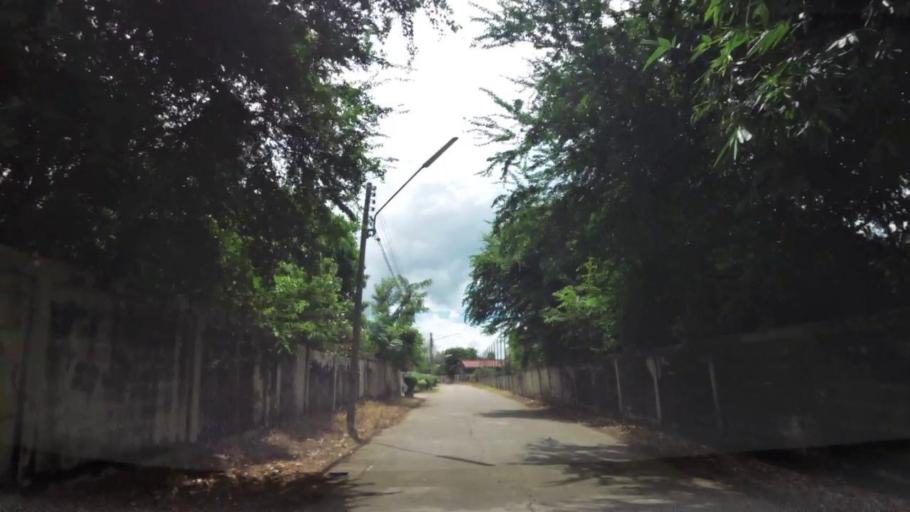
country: TH
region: Nakhon Sawan
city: Phai Sali
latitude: 15.5971
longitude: 100.6513
